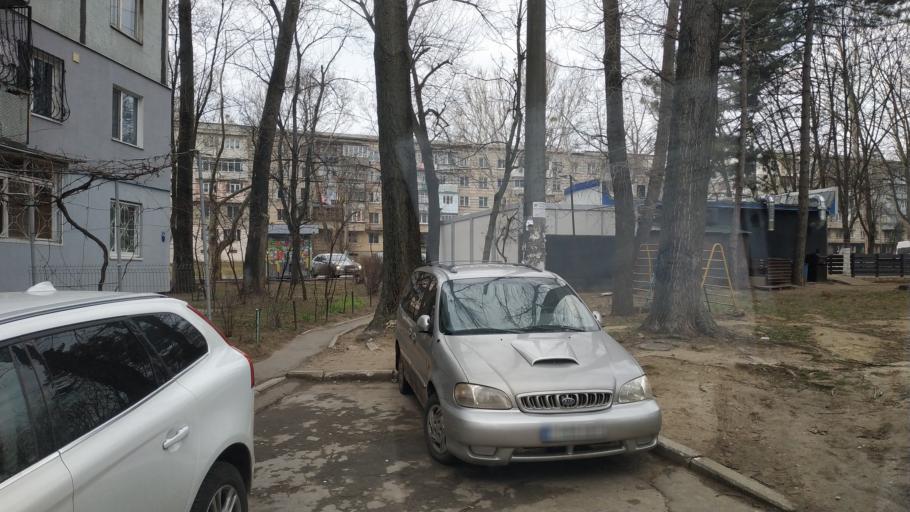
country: MD
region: Chisinau
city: Chisinau
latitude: 47.0283
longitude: 28.7916
